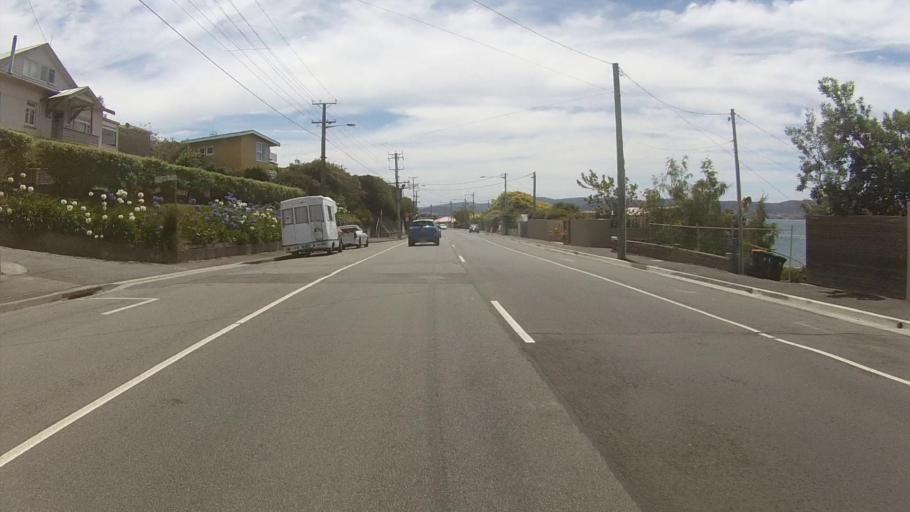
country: AU
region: Tasmania
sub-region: Kingborough
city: Taroona
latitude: -42.9213
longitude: 147.3600
